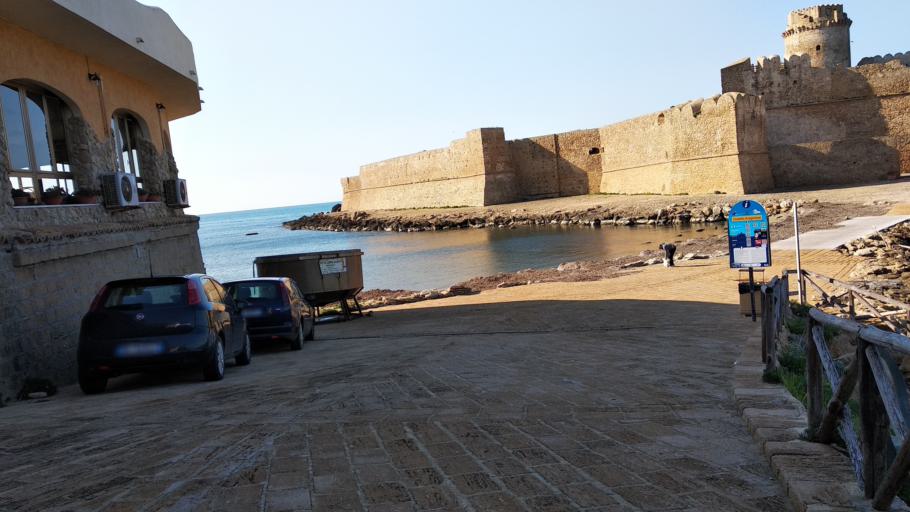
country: IT
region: Calabria
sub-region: Provincia di Crotone
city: Le Castella
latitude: 38.9080
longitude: 17.0222
